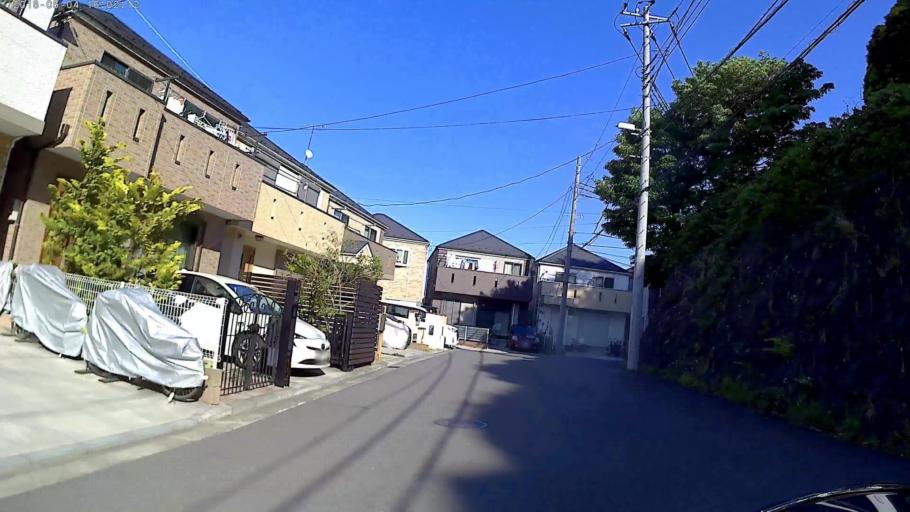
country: JP
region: Kanagawa
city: Yokohama
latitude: 35.4930
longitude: 139.6610
